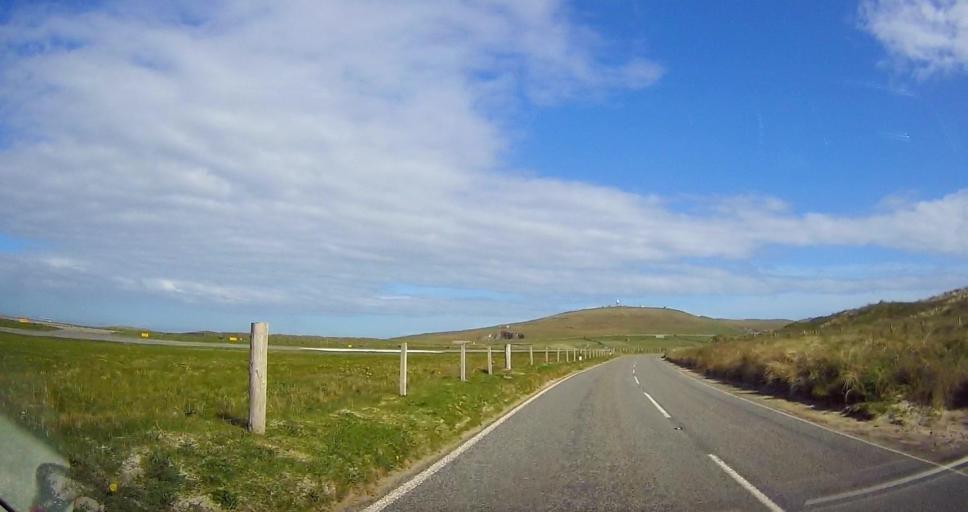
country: GB
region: Scotland
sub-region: Shetland Islands
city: Sandwick
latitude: 59.8761
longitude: -1.2935
